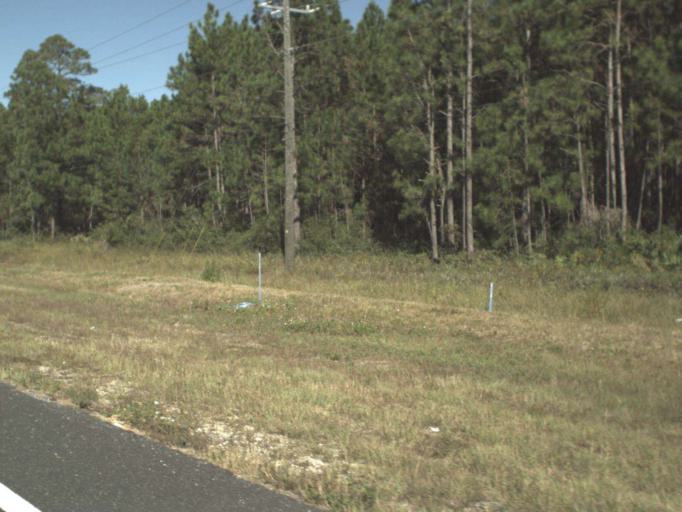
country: US
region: Florida
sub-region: Walton County
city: Seaside
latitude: 30.3697
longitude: -86.1960
